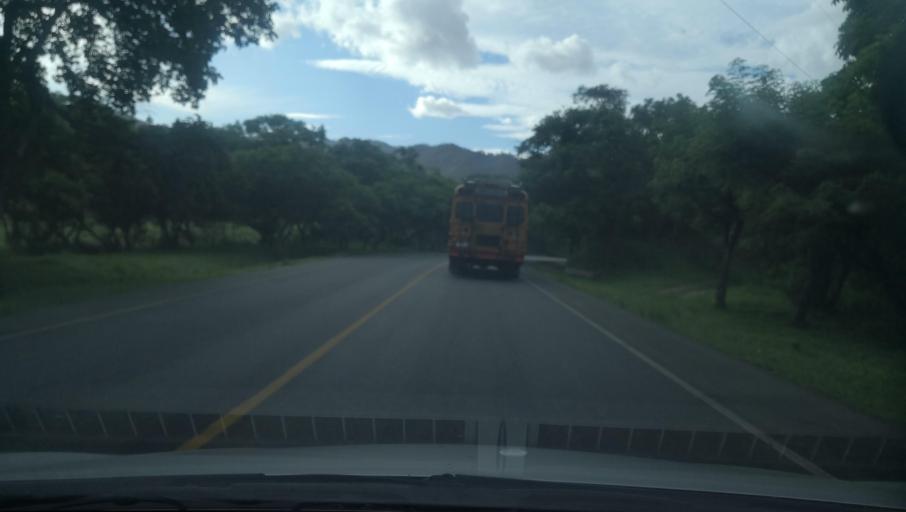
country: NI
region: Nueva Segovia
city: Ocotal
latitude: 13.6743
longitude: -86.4874
